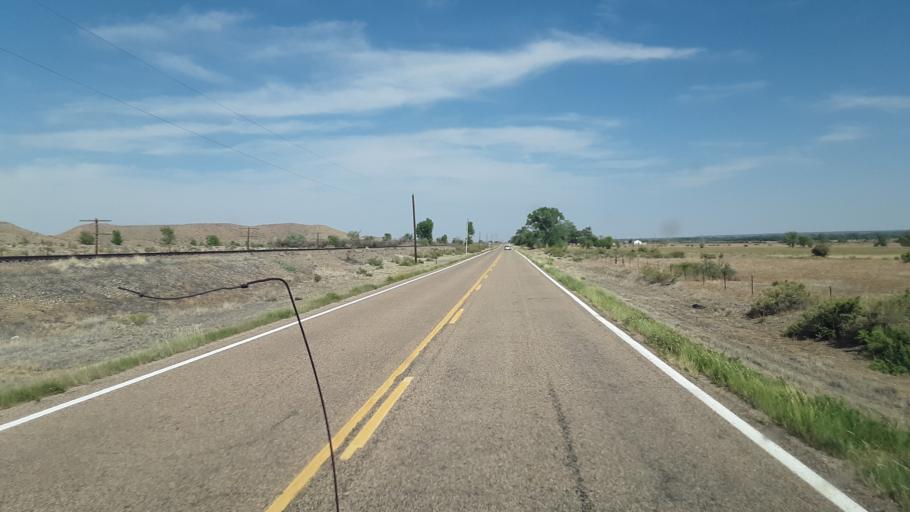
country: US
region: Colorado
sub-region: Otero County
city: Fowler
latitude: 38.1636
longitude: -104.0553
